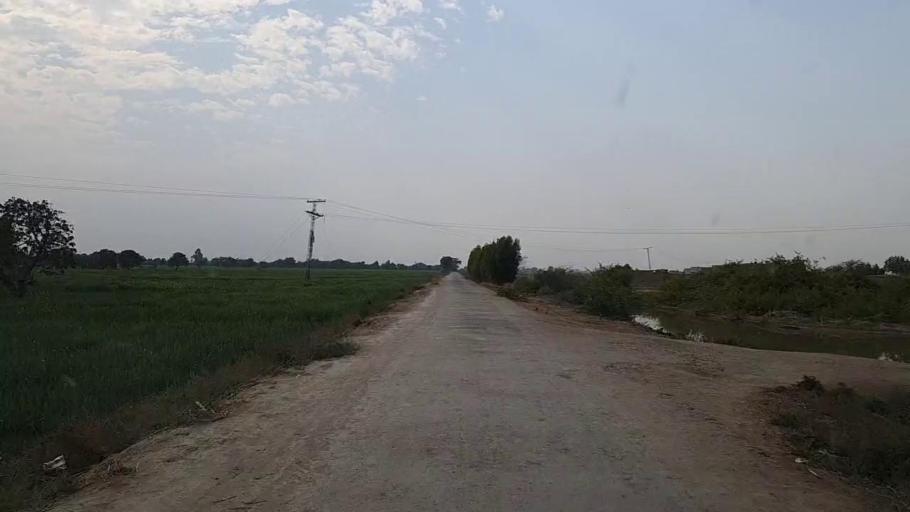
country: PK
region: Sindh
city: Mirwah Gorchani
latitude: 25.3717
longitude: 69.0809
